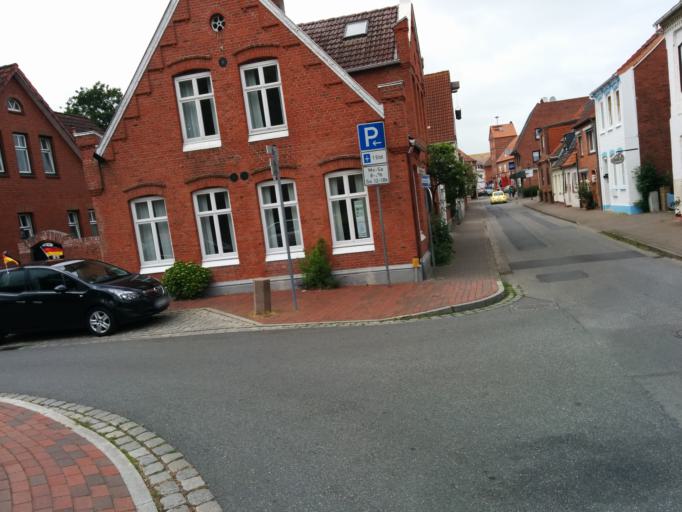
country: DE
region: Schleswig-Holstein
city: Tonning
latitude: 54.3162
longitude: 8.9430
